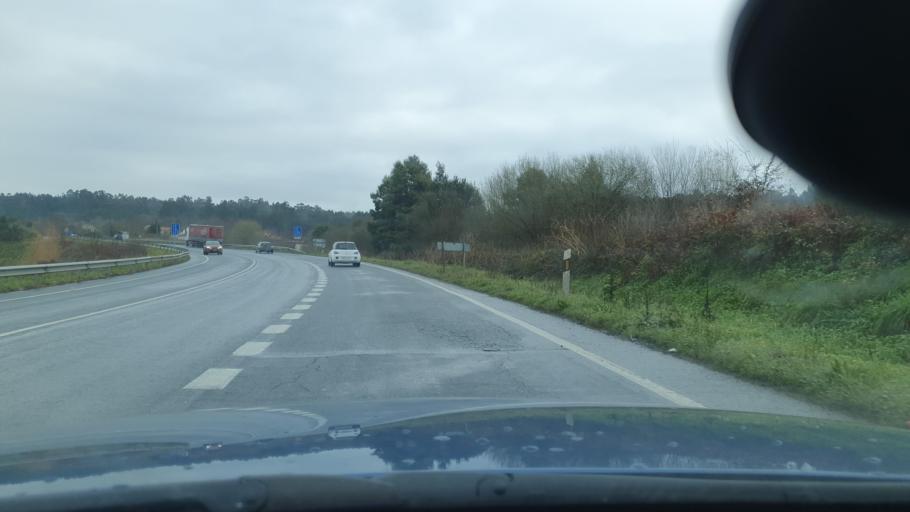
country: ES
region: Galicia
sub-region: Provincia da Coruna
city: Padron
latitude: 42.8091
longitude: -8.6244
